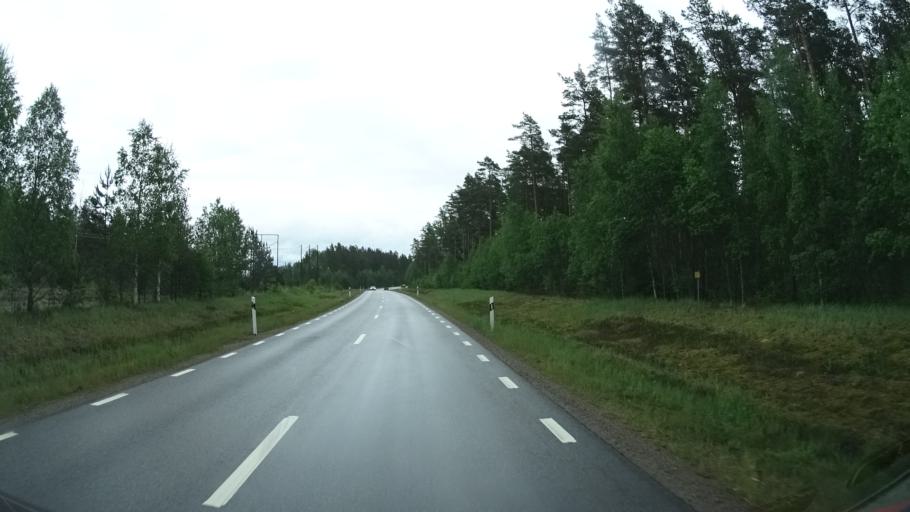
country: SE
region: Kalmar
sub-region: Hultsfreds Kommun
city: Hultsfred
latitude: 57.5133
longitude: 15.8273
